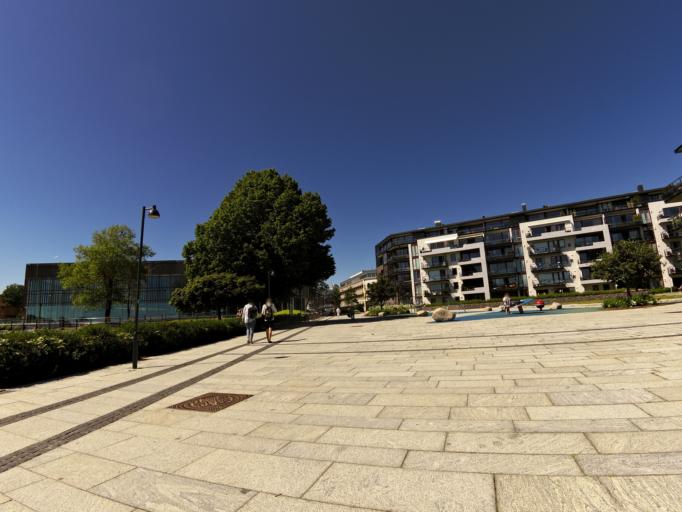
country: NO
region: Vest-Agder
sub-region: Kristiansand
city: Kristiansand
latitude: 58.1462
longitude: 8.0084
